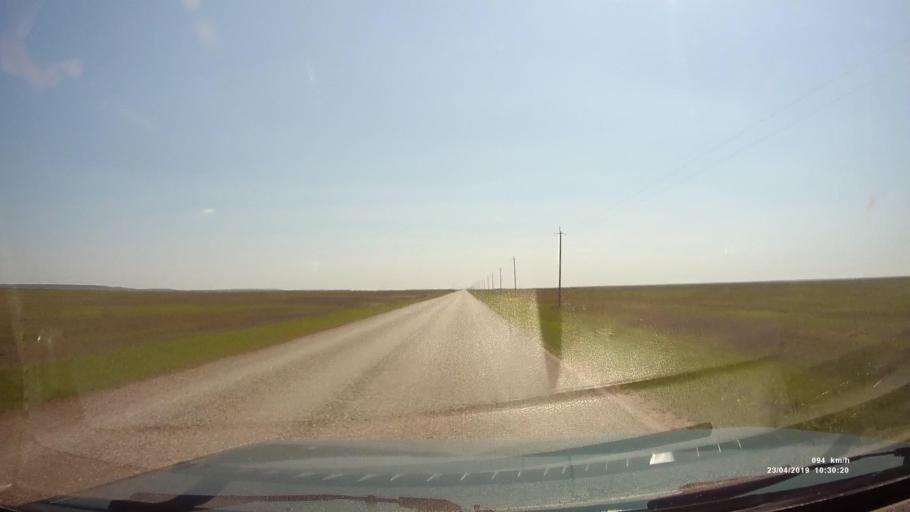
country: RU
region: Kalmykiya
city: Yashalta
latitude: 46.5928
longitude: 42.5426
